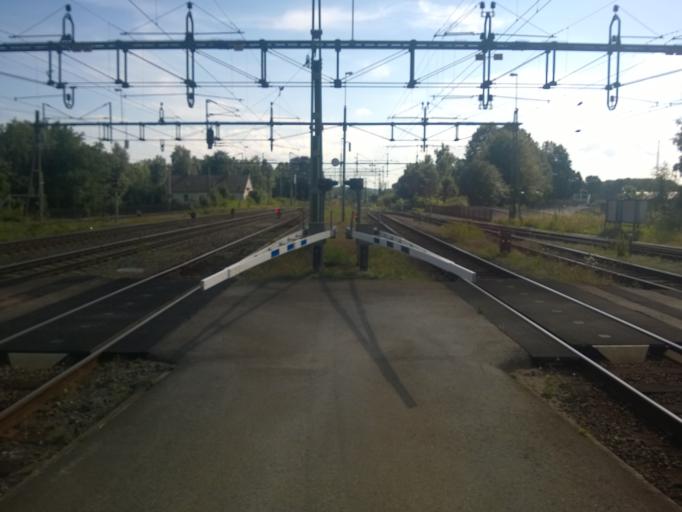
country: SE
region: Skane
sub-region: Hassleholms Kommun
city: Hassleholm
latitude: 56.1556
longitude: 13.7619
